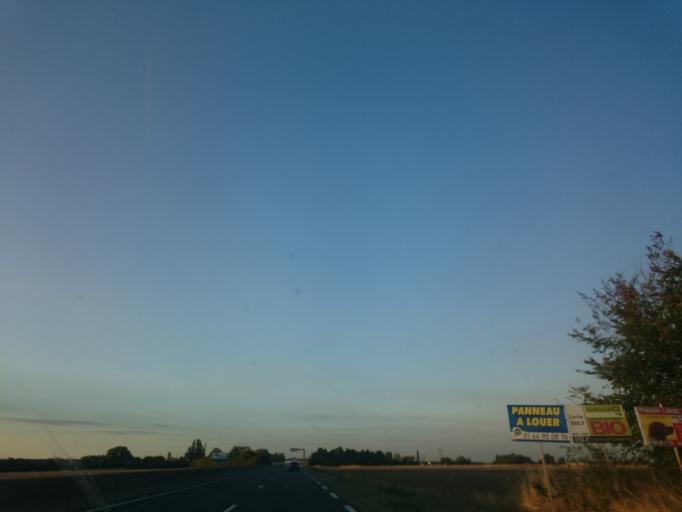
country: FR
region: Ile-de-France
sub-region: Departement de l'Essonne
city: Boissy-sous-Saint-Yon
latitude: 48.5550
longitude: 2.2220
